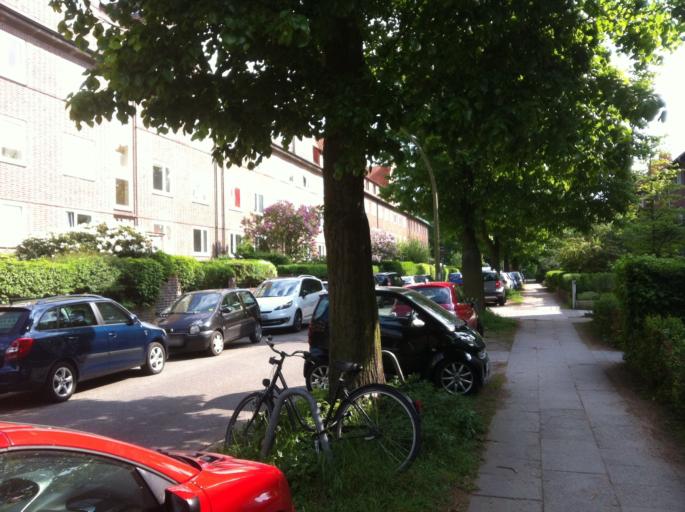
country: DE
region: Hamburg
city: Altona
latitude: 53.5526
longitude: 9.9095
